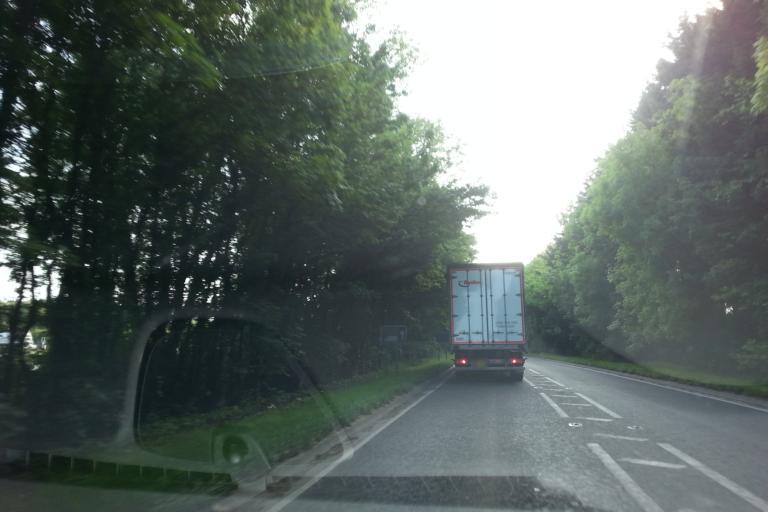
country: GB
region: England
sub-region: Cambridgeshire
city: Hemingford Grey
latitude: 52.3179
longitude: -0.0771
